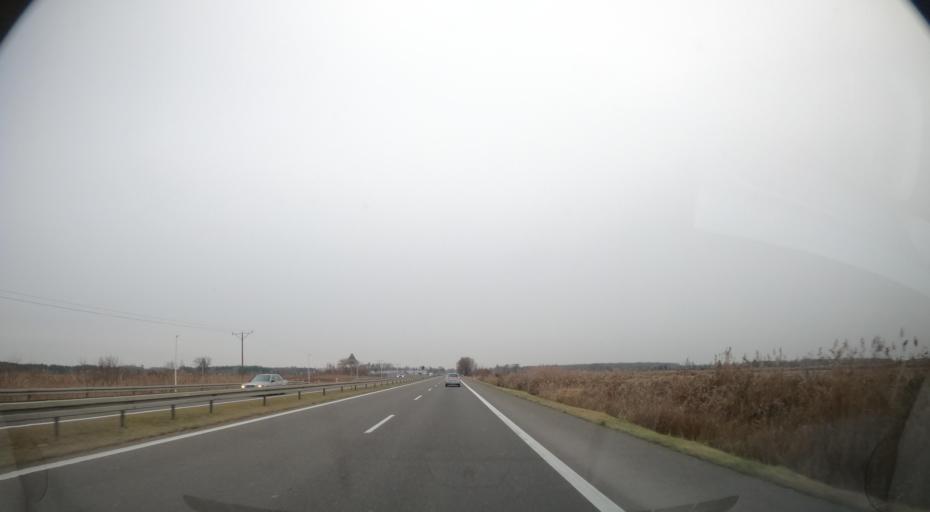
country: PL
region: Masovian Voivodeship
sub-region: Powiat radomski
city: Jedlinsk
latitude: 51.5015
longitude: 21.1188
